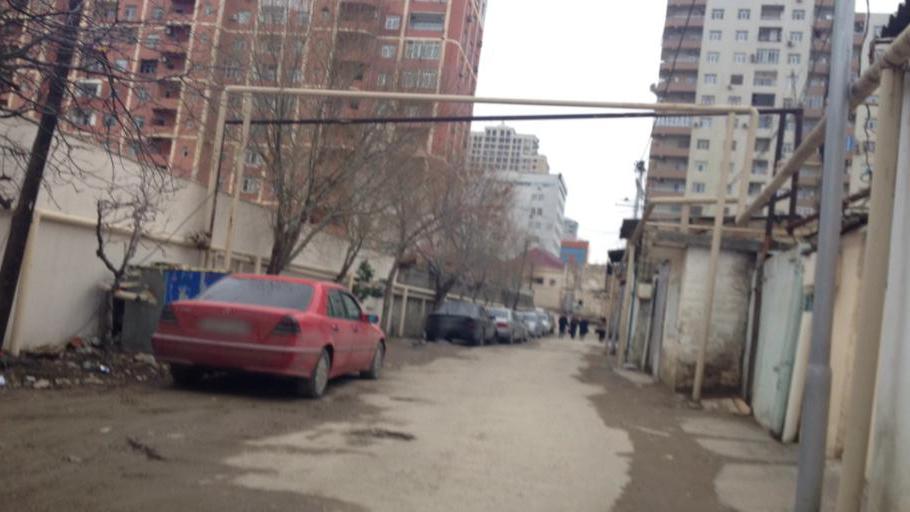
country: AZ
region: Baki
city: Khodzhi-Gasan
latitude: 40.3909
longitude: 49.8113
